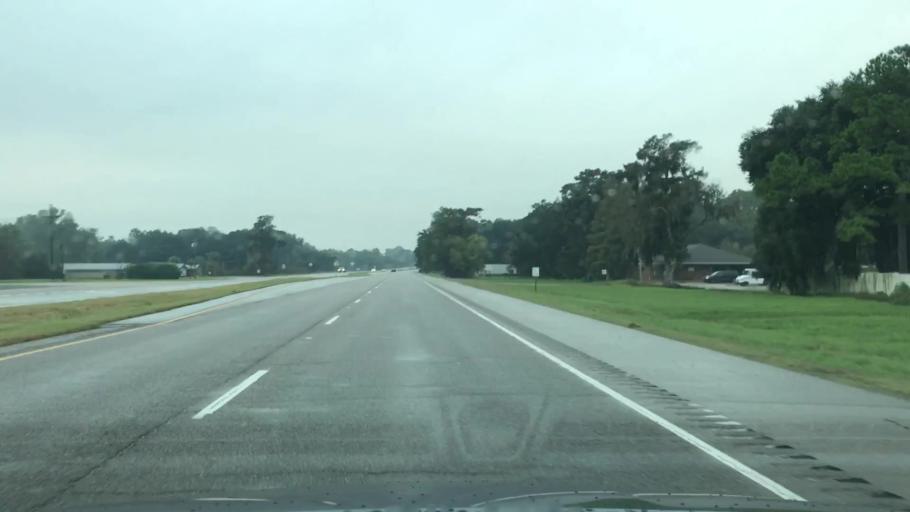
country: US
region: Louisiana
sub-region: Saint Charles Parish
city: Des Allemands
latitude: 29.8243
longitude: -90.4668
